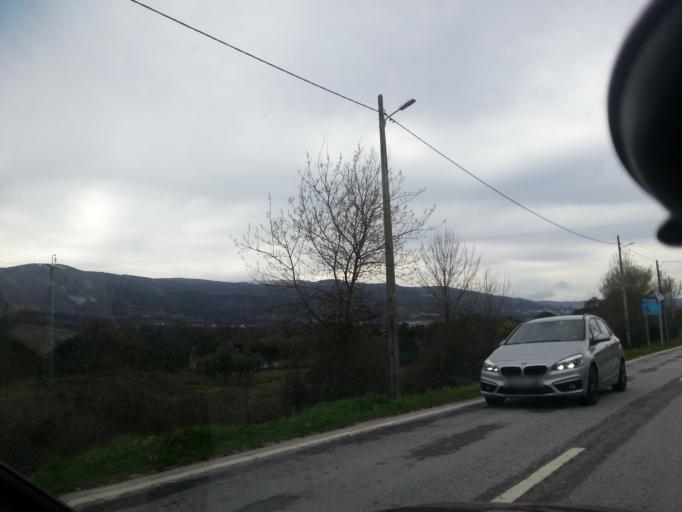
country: PT
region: Guarda
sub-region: Seia
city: Seia
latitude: 40.4758
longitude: -7.6700
